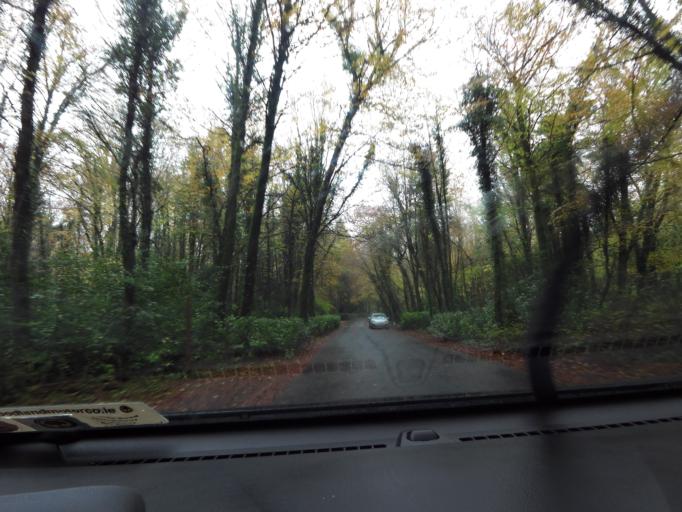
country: IE
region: Connaught
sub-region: County Galway
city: Gort
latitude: 53.0891
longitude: -8.8343
